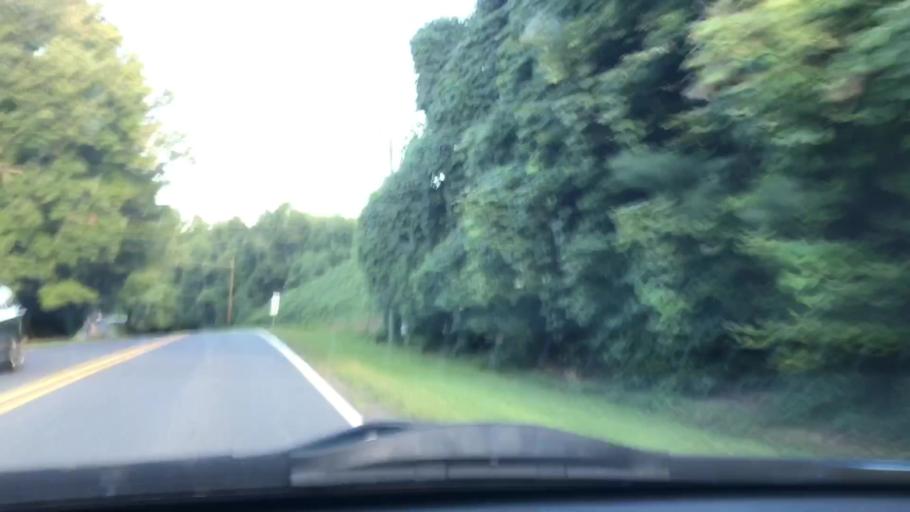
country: US
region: North Carolina
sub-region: Randolph County
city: Asheboro
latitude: 35.7150
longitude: -79.8181
